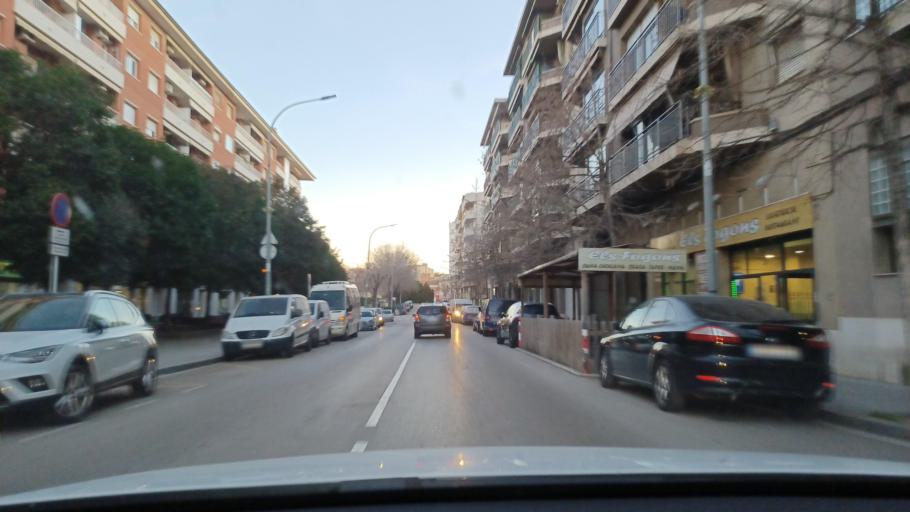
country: ES
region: Catalonia
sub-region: Provincia de Barcelona
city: Vilafranca del Penedes
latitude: 41.3445
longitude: 1.6929
